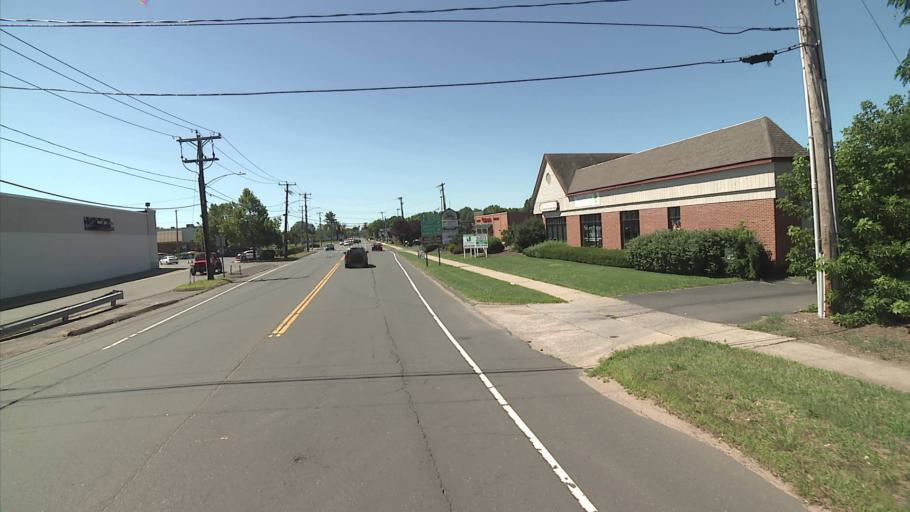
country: US
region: Connecticut
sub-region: Hartford County
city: Plainville
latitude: 41.6757
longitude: -72.8578
